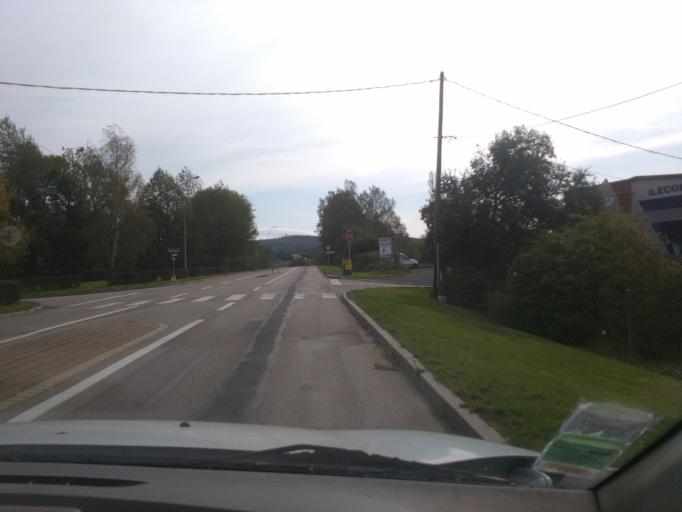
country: FR
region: Lorraine
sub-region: Departement des Vosges
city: Jeanmenil
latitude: 48.3337
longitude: 6.6983
